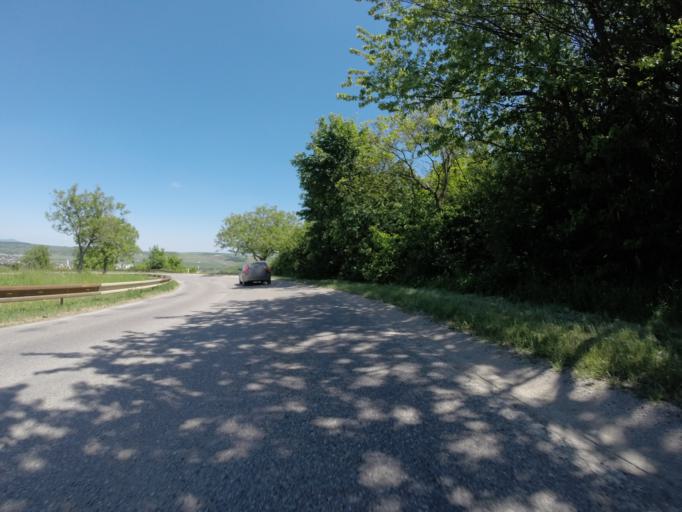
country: SK
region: Trnavsky
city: Hlohovec
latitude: 48.4136
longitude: 17.7956
